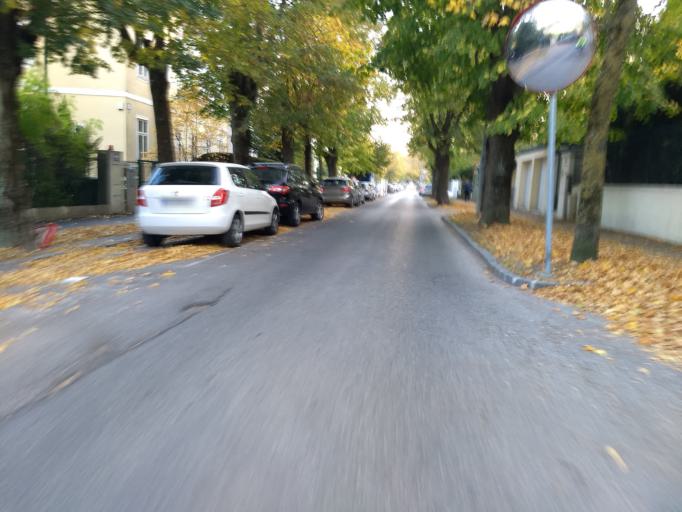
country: AT
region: Lower Austria
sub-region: Politischer Bezirk Modling
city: Perchtoldsdorf
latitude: 48.1269
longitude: 16.2573
